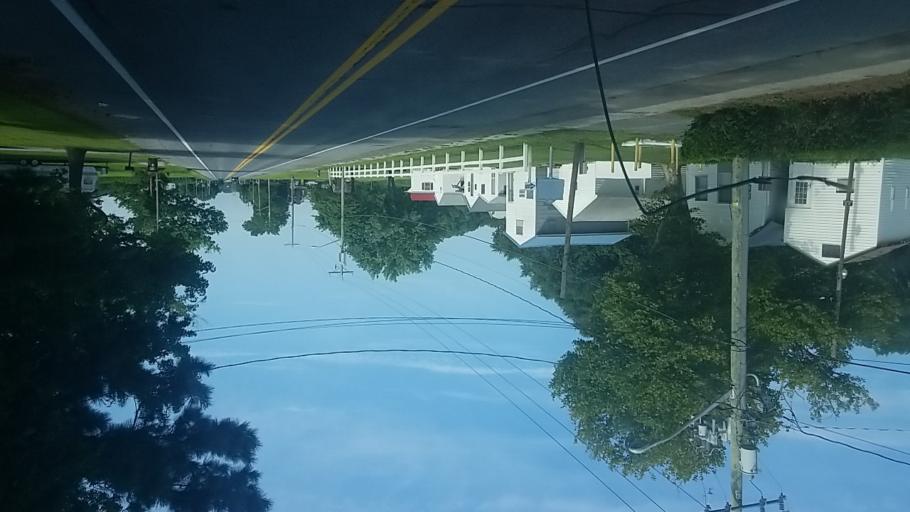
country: US
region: Delaware
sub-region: Sussex County
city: Selbyville
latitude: 38.5313
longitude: -75.2355
